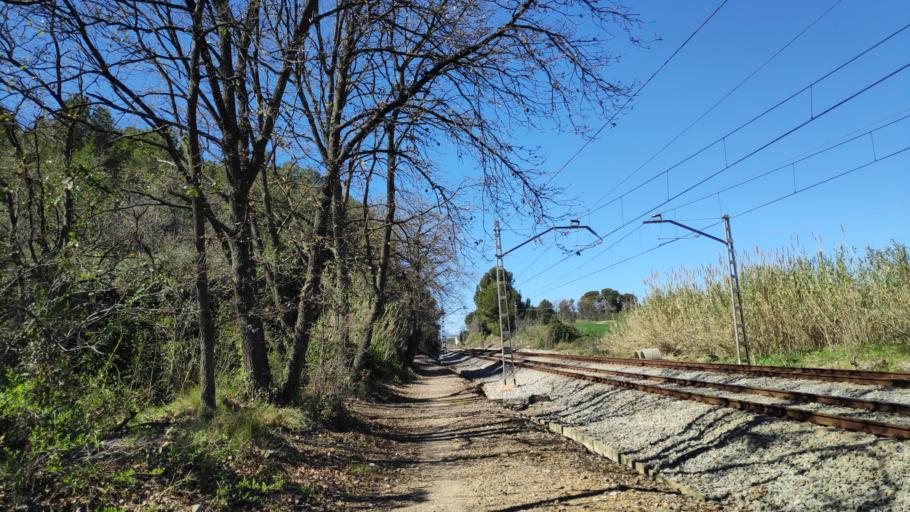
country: ES
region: Catalonia
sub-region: Provincia de Barcelona
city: Sant Quirze del Valles
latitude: 41.5645
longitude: 2.0695
